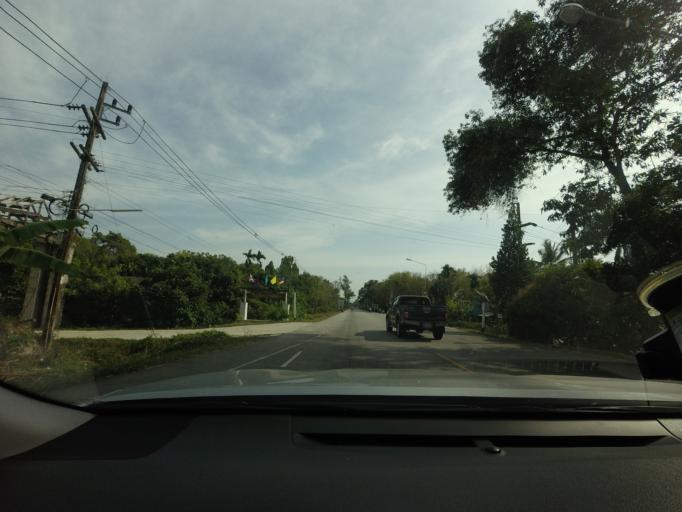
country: TH
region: Narathiwat
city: Ra-ngae
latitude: 6.3331
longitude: 101.7894
